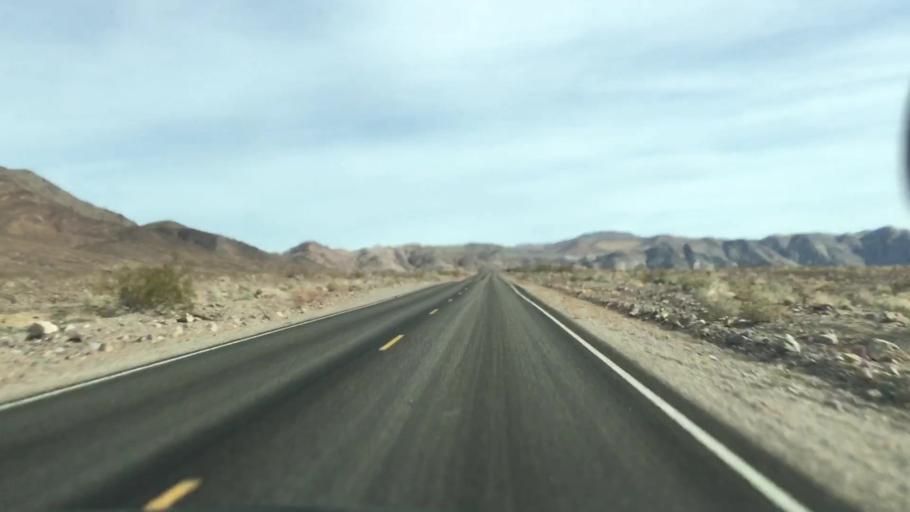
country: US
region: Nevada
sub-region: Nye County
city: Beatty
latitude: 36.7075
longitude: -116.9903
